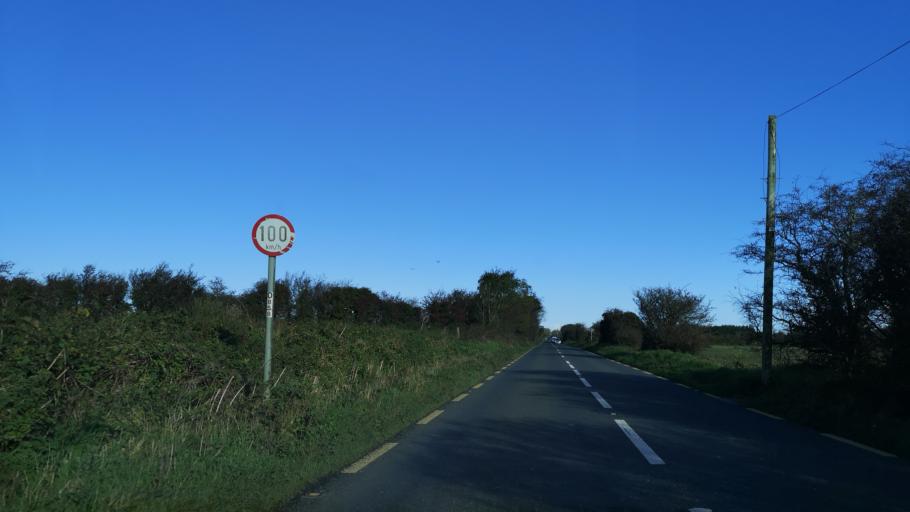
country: IE
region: Connaught
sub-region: County Galway
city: Claregalway
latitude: 53.3656
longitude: -9.0172
